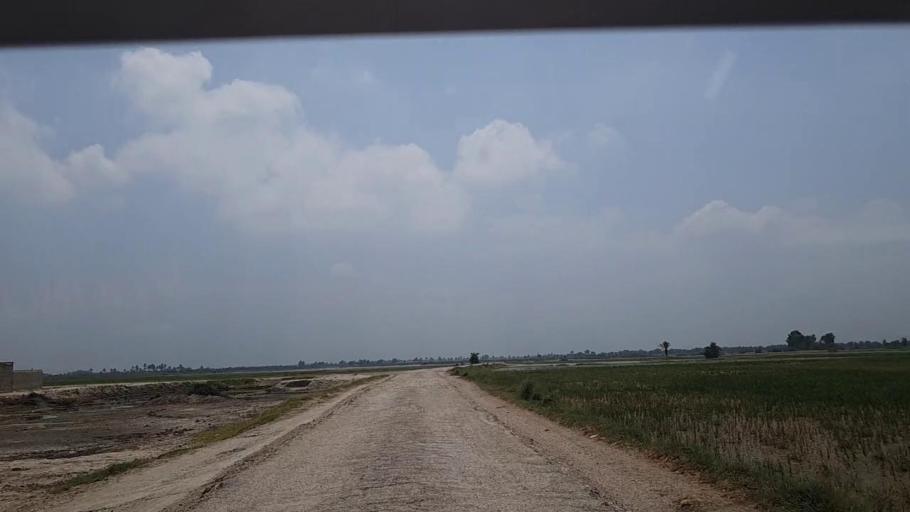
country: PK
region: Sindh
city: Khanpur
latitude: 27.9010
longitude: 69.3911
